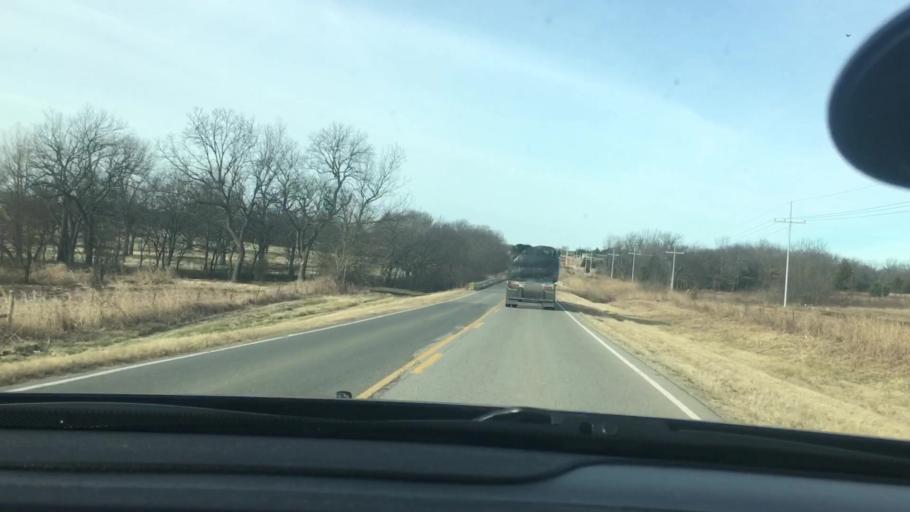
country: US
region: Oklahoma
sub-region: Garvin County
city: Stratford
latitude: 34.7967
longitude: -96.8886
